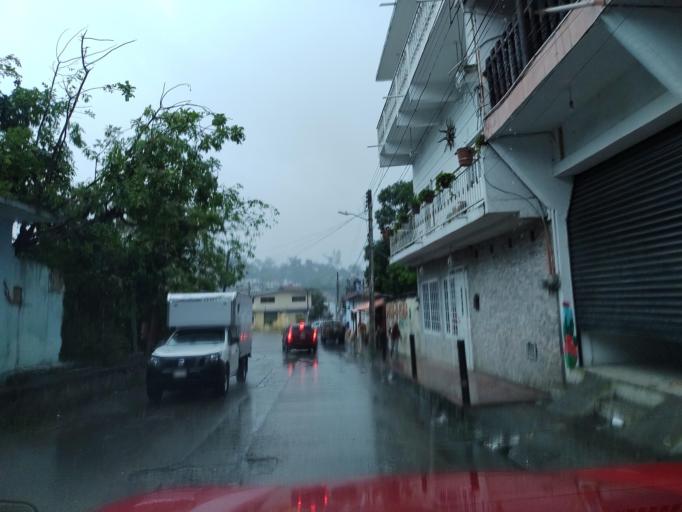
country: MX
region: Veracruz
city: Papantla de Olarte
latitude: 20.4471
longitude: -97.3262
